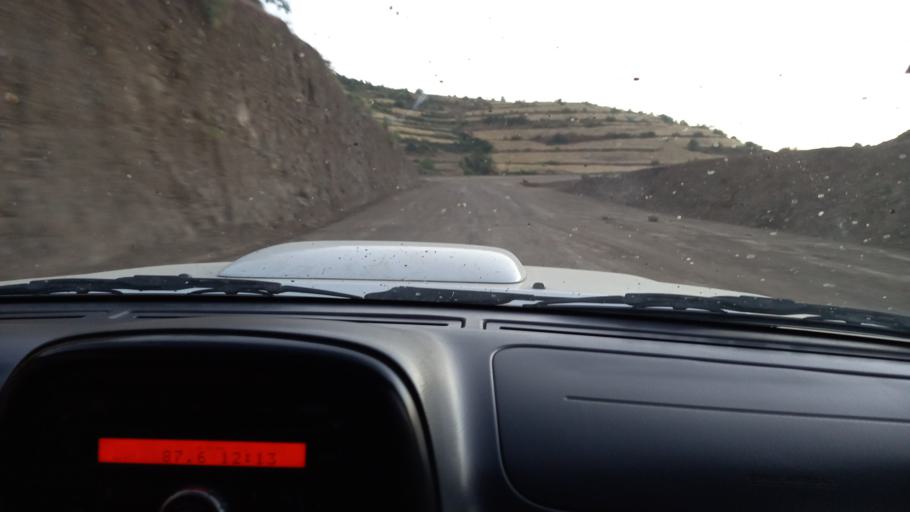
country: ET
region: Amhara
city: Debark'
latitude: 13.0352
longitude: 38.0555
